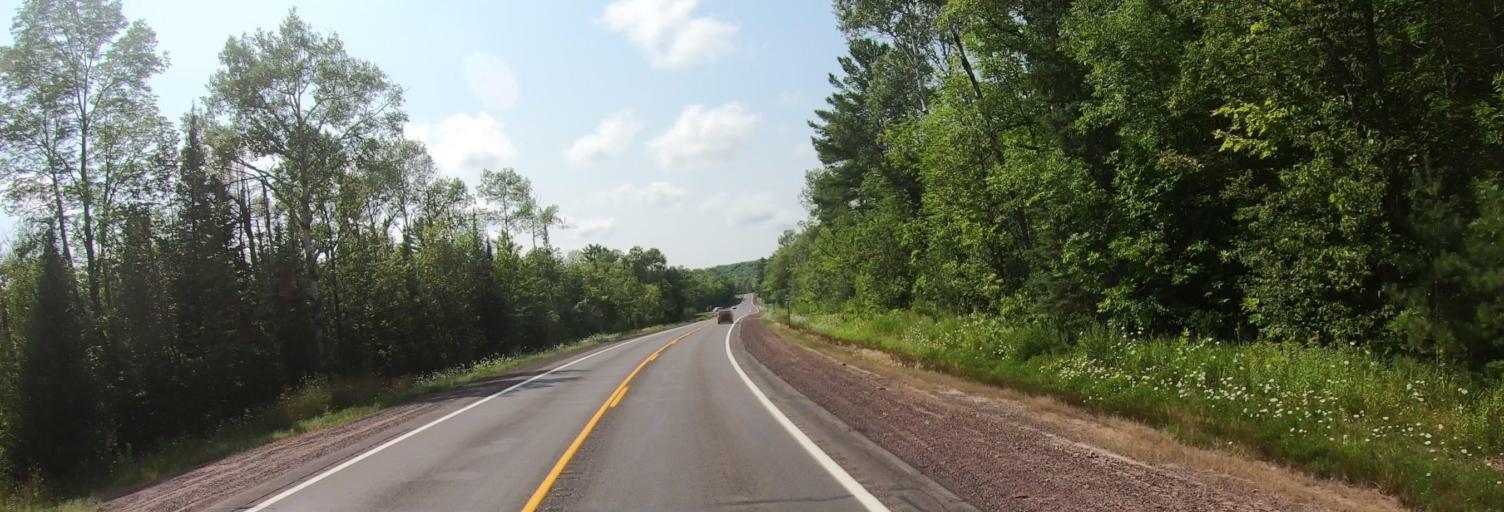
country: US
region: Michigan
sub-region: Ontonagon County
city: Ontonagon
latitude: 46.7297
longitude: -89.1431
